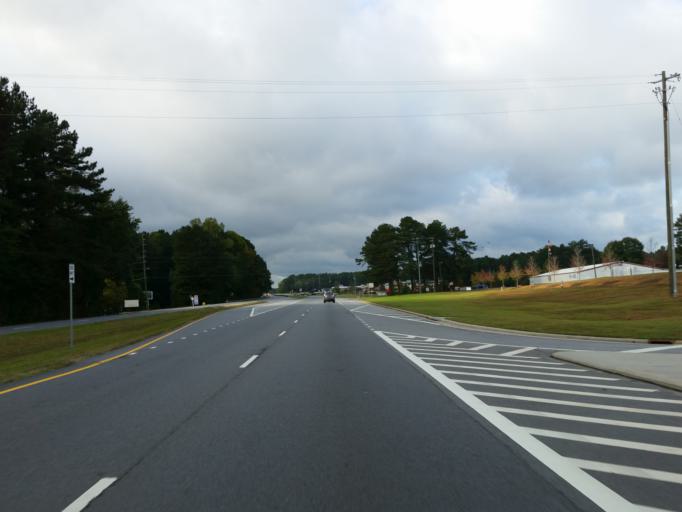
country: US
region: Georgia
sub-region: Cobb County
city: Acworth
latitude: 34.0690
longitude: -84.7253
